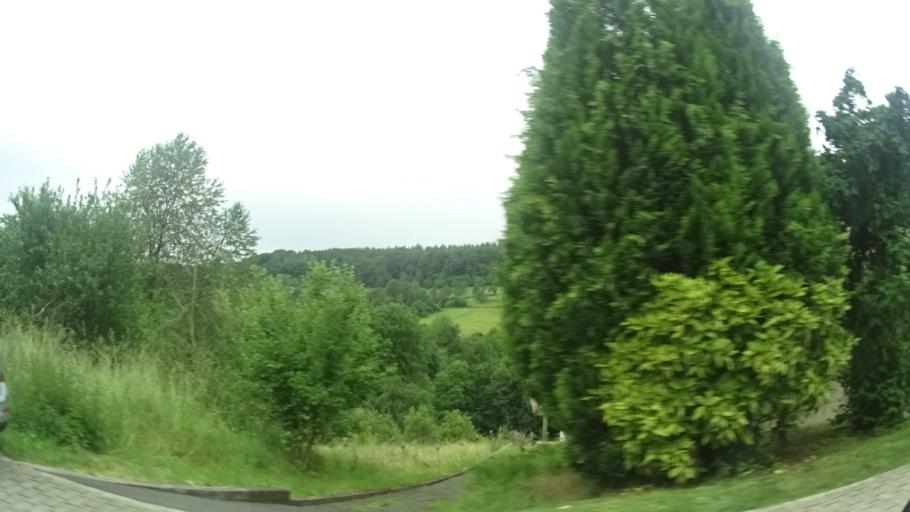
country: DE
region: Bavaria
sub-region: Regierungsbezirk Unterfranken
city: Johannesberg
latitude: 50.0641
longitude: 9.1265
